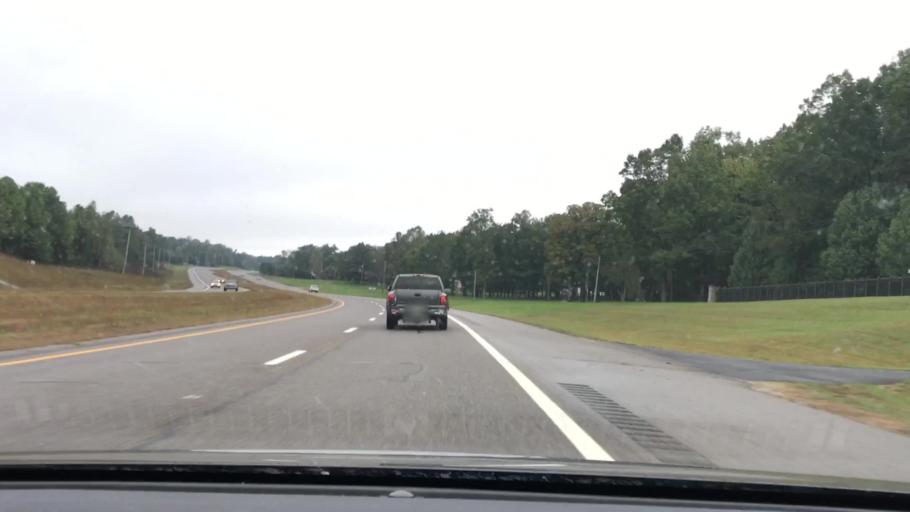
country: US
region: Tennessee
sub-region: Fentress County
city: Jamestown
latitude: 36.3689
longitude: -84.9439
